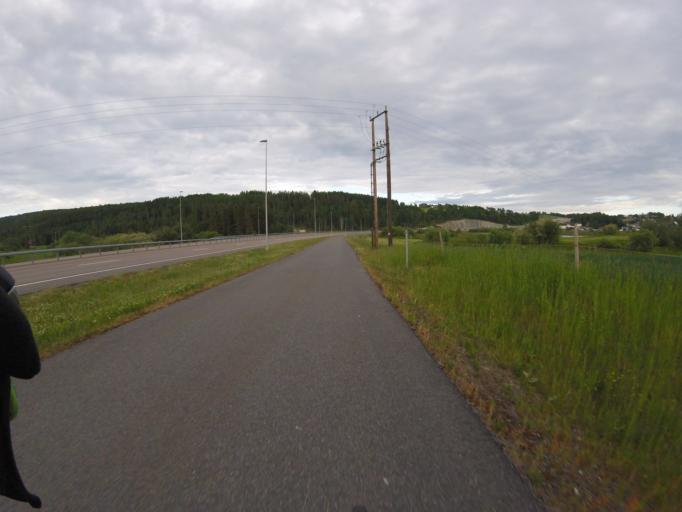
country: NO
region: Akershus
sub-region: Fet
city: Fetsund
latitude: 59.9408
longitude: 11.1246
